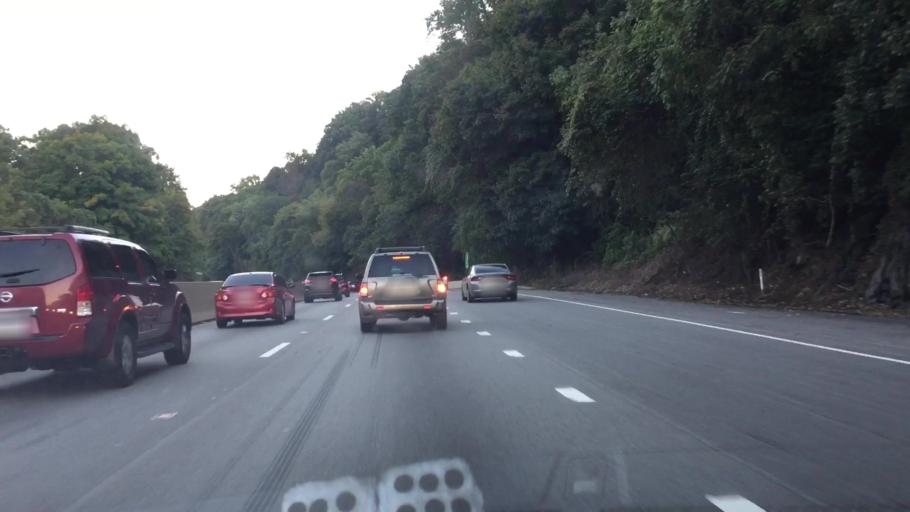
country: US
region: Pennsylvania
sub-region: Montgomery County
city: Narberth
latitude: 40.0386
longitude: -75.2490
